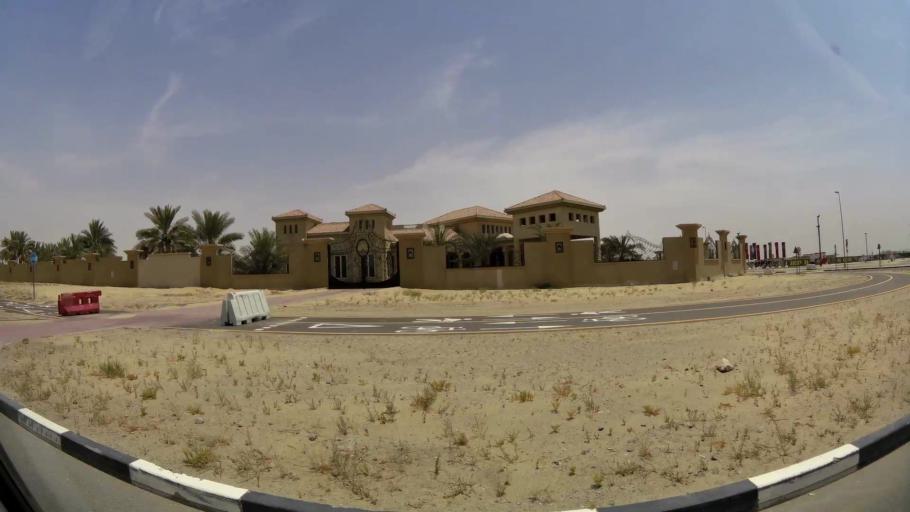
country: AE
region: Ash Shariqah
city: Sharjah
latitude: 25.2354
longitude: 55.4770
